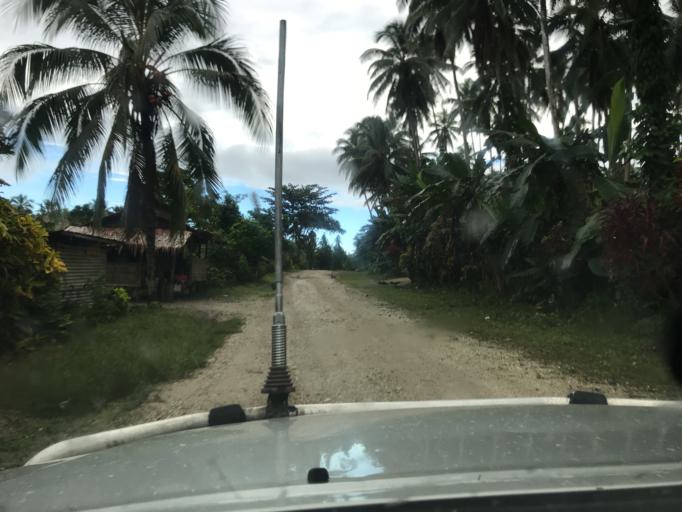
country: SB
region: Malaita
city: Auki
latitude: -8.4835
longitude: 160.6789
